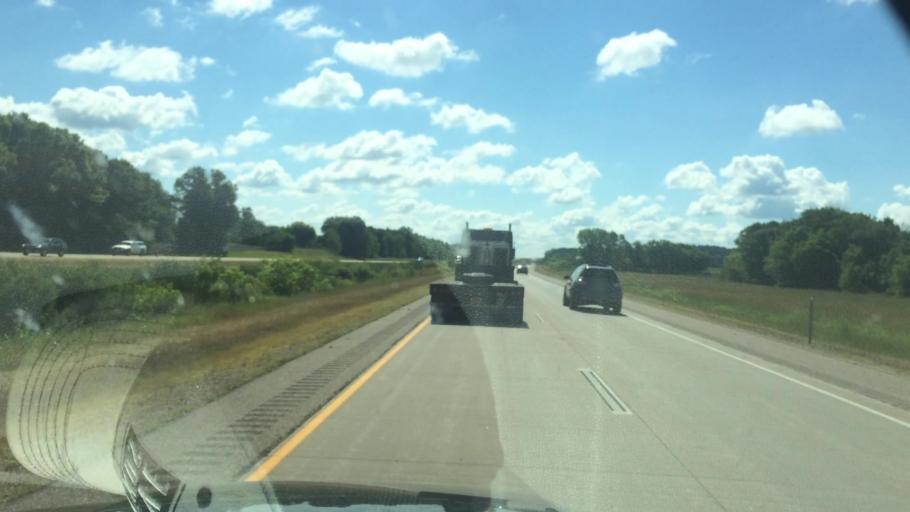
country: US
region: Wisconsin
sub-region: Portage County
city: Amherst
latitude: 44.3989
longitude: -89.2133
